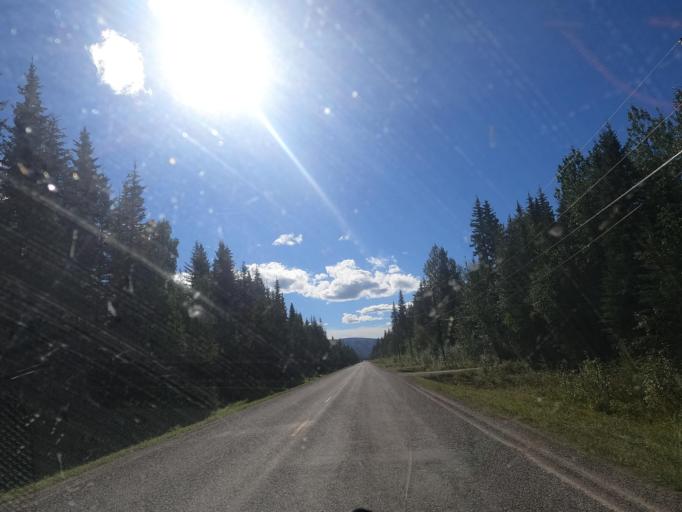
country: CA
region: Yukon
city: Dawson City
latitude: 64.0577
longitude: -139.0883
